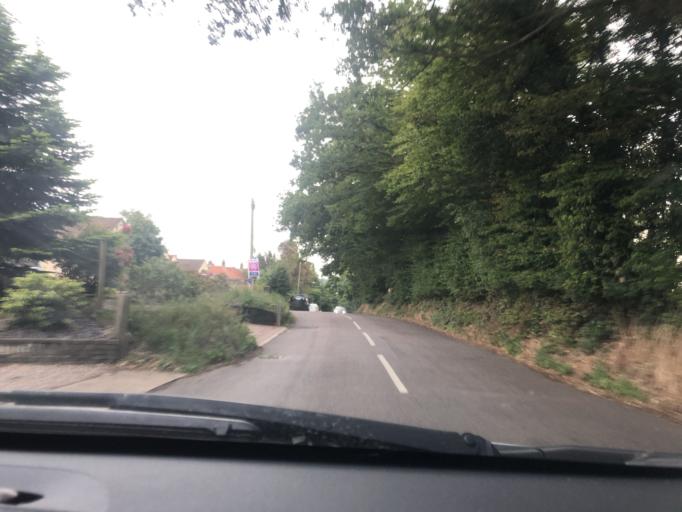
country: GB
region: England
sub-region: Kent
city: Sturry
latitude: 51.3091
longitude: 1.1355
